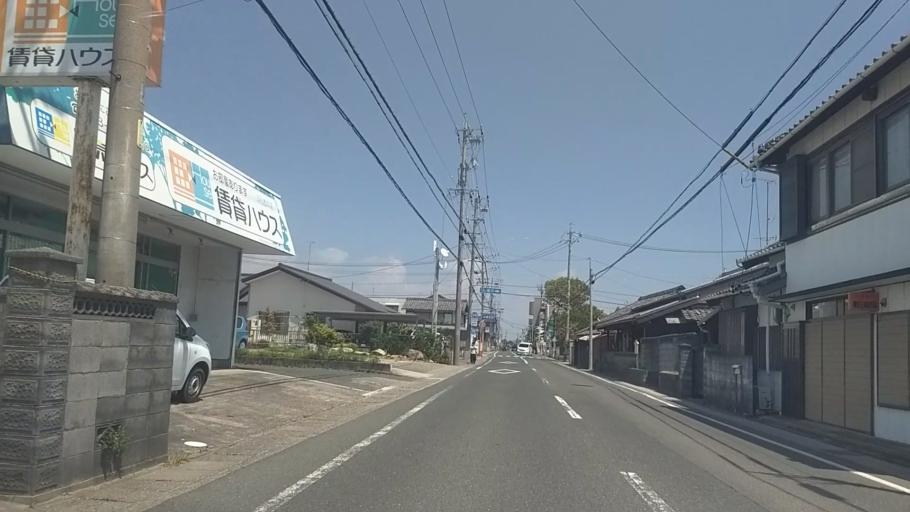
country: JP
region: Shizuoka
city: Hamamatsu
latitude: 34.6869
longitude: 137.6690
